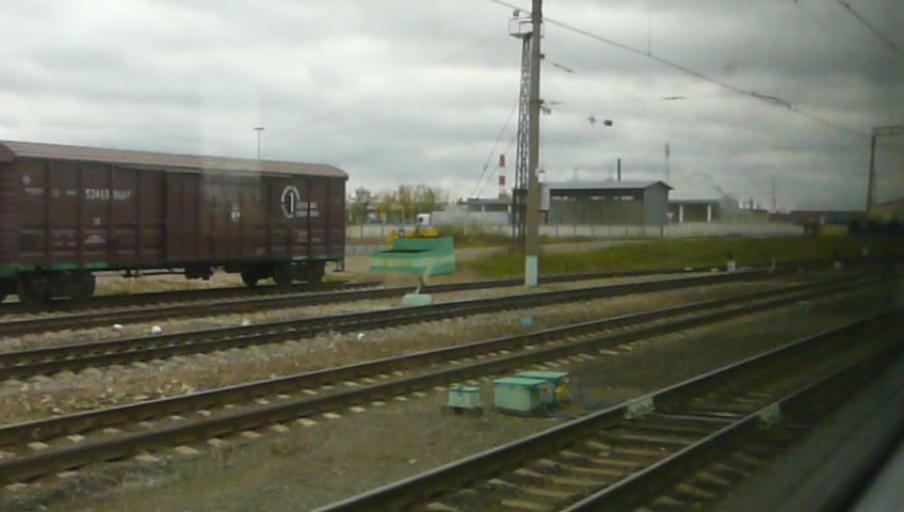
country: RU
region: Moskovskaya
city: Yegor'yevsk
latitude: 55.3922
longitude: 39.0076
